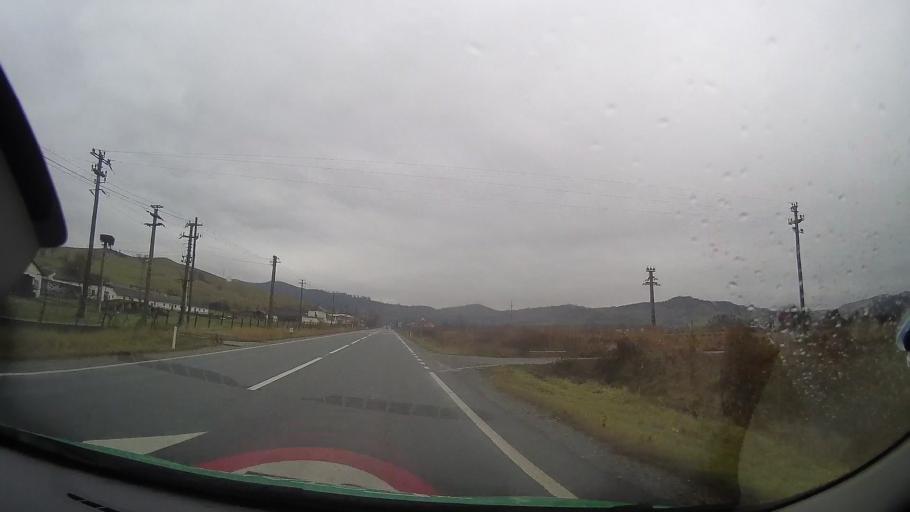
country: RO
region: Bistrita-Nasaud
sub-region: Comuna Teaca
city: Teaca
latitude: 46.9198
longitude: 24.4920
